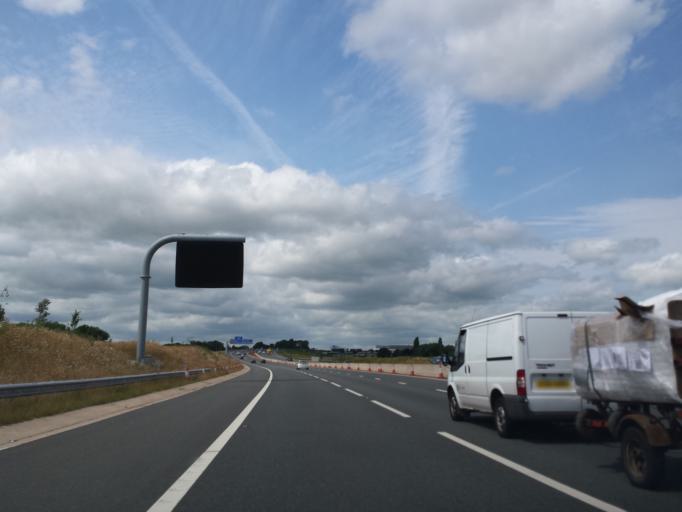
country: GB
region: England
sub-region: North Yorkshire
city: Bedale
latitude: 54.2961
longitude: -1.5568
